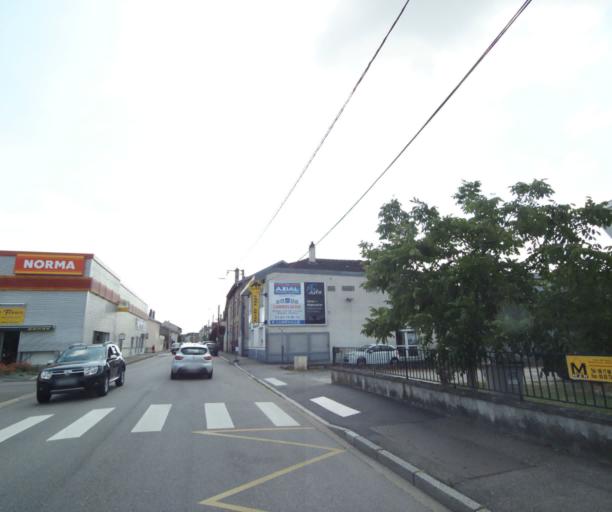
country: FR
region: Lorraine
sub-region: Departement de Meurthe-et-Moselle
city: Luneville
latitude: 48.5876
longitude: 6.4842
